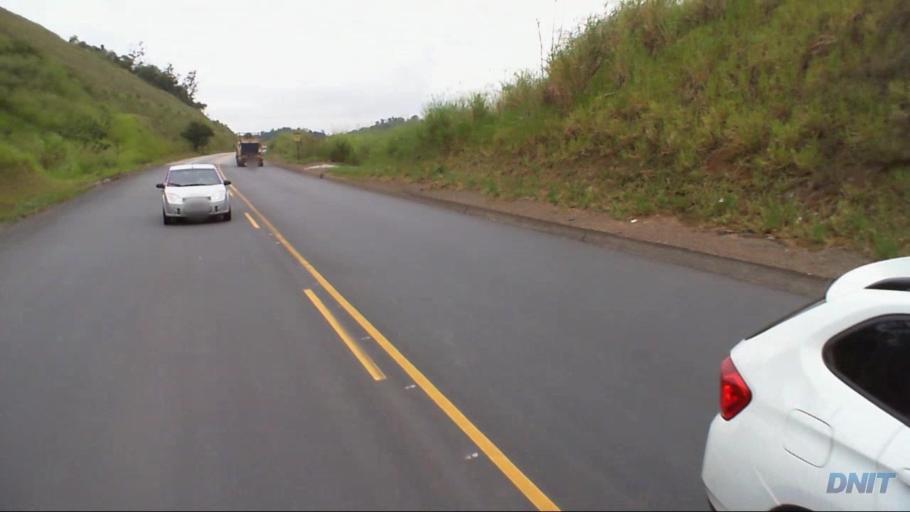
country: BR
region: Minas Gerais
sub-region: Coronel Fabriciano
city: Coronel Fabriciano
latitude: -19.5322
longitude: -42.5851
